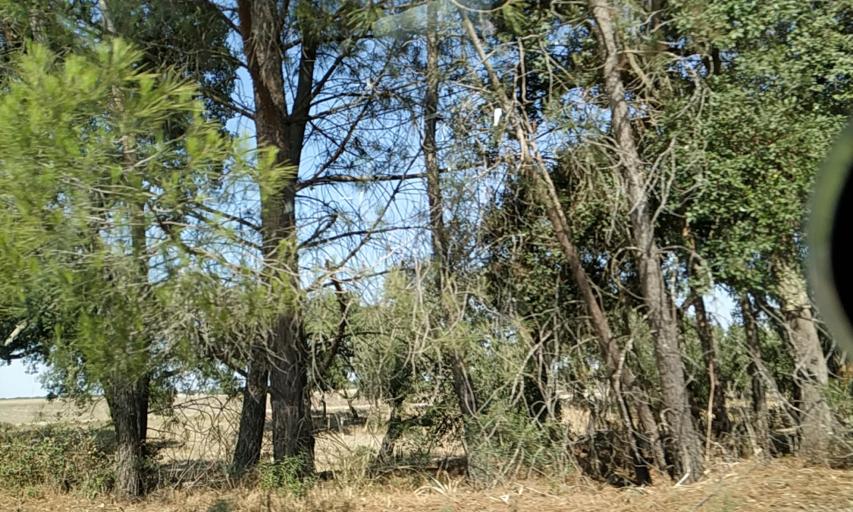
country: PT
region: Santarem
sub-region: Benavente
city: Poceirao
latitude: 38.7490
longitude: -8.6318
